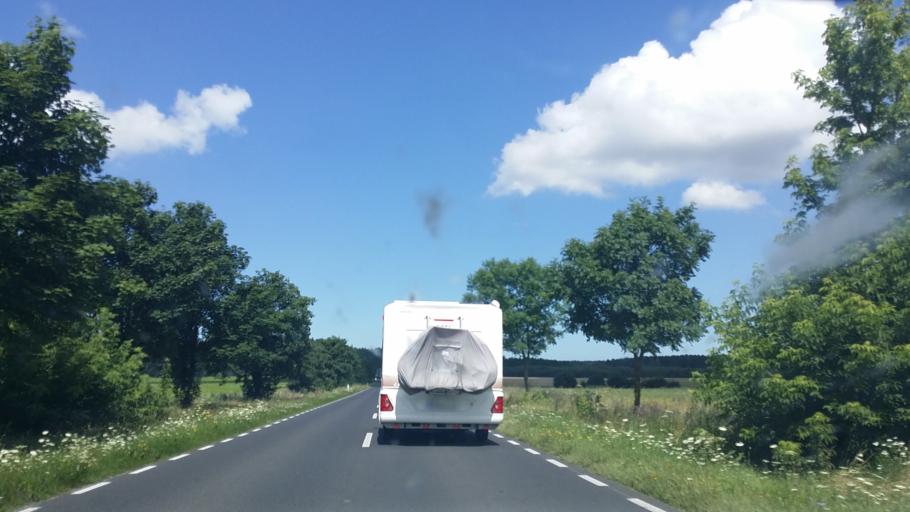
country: PL
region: West Pomeranian Voivodeship
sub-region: Powiat kolobrzeski
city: Goscino
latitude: 54.0905
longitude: 15.6237
